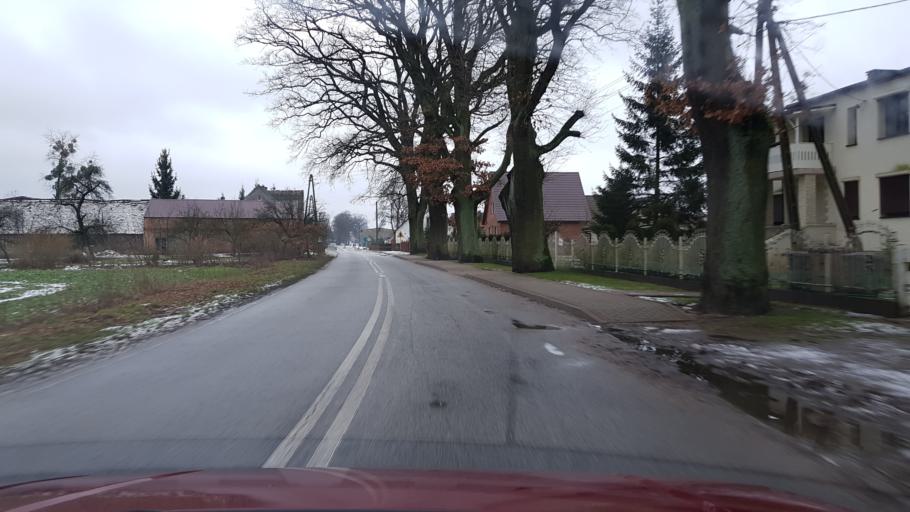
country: PL
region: West Pomeranian Voivodeship
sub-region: Powiat gryficki
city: Ploty
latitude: 53.7085
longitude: 15.2750
